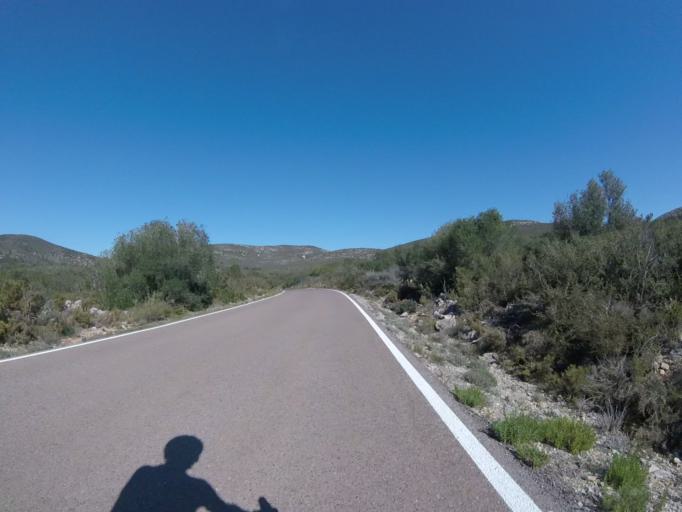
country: ES
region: Valencia
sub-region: Provincia de Castello
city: Santa Magdalena de Pulpis
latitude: 40.3765
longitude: 0.2715
